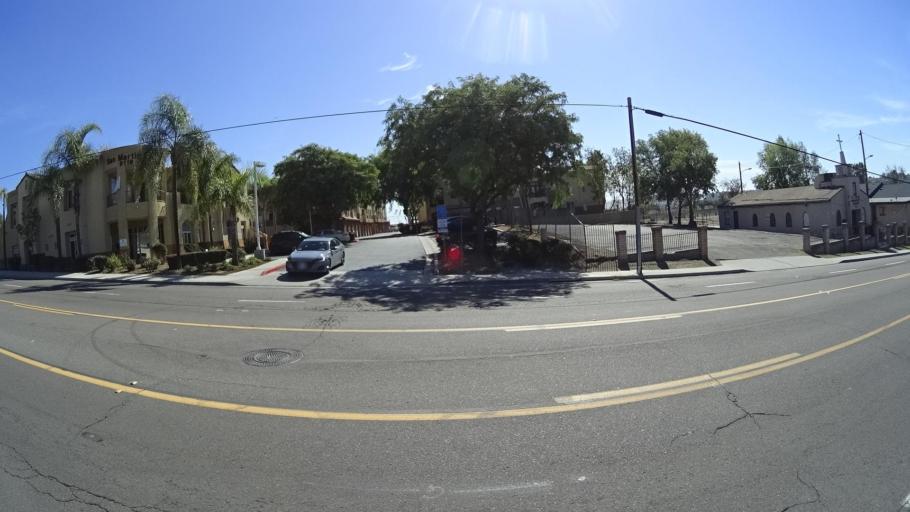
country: US
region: California
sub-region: San Diego County
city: La Presa
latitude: 32.7149
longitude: -117.0035
